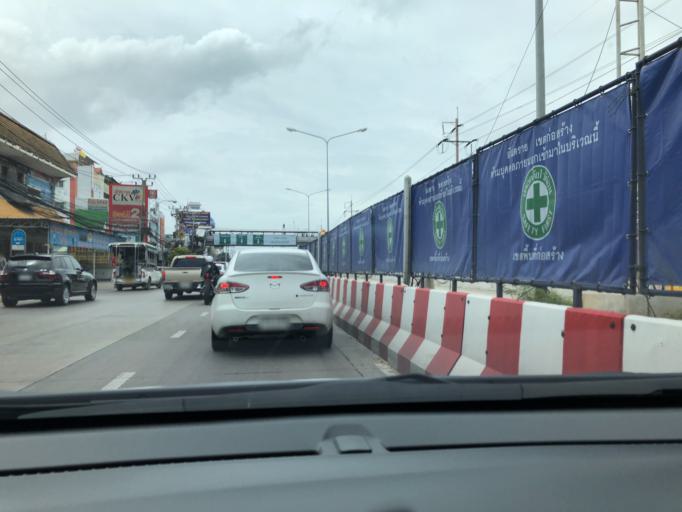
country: TH
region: Bangkok
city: Bang Na
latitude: 13.6917
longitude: 100.6469
